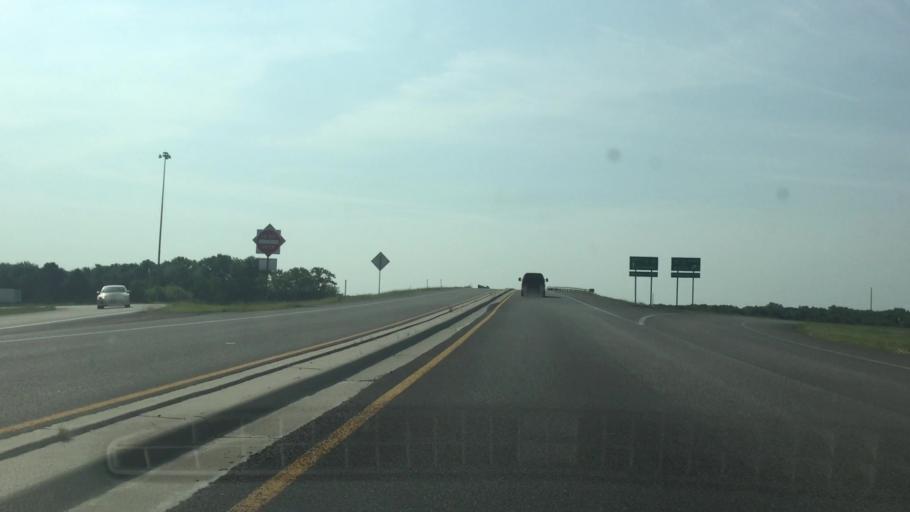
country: US
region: Kansas
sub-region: Butler County
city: Andover
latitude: 37.6882
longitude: -97.1820
